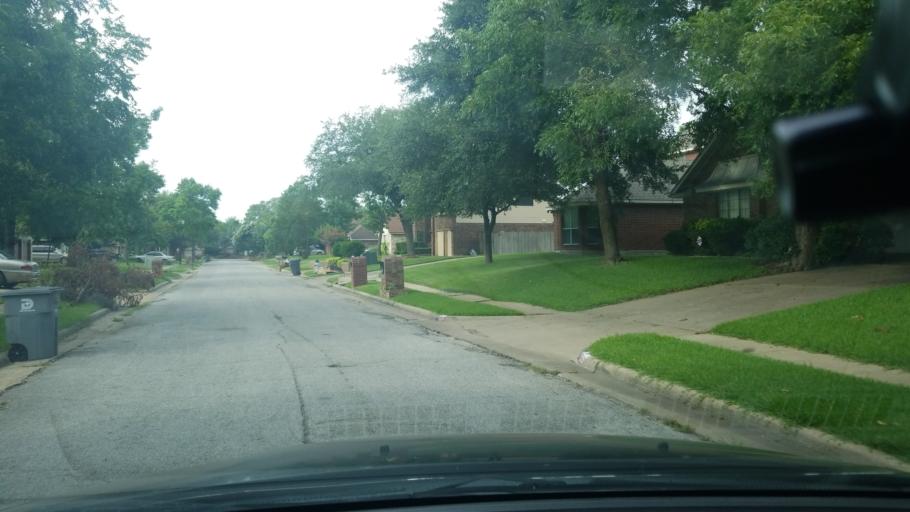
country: US
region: Texas
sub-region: Dallas County
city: Balch Springs
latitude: 32.7403
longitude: -96.6641
